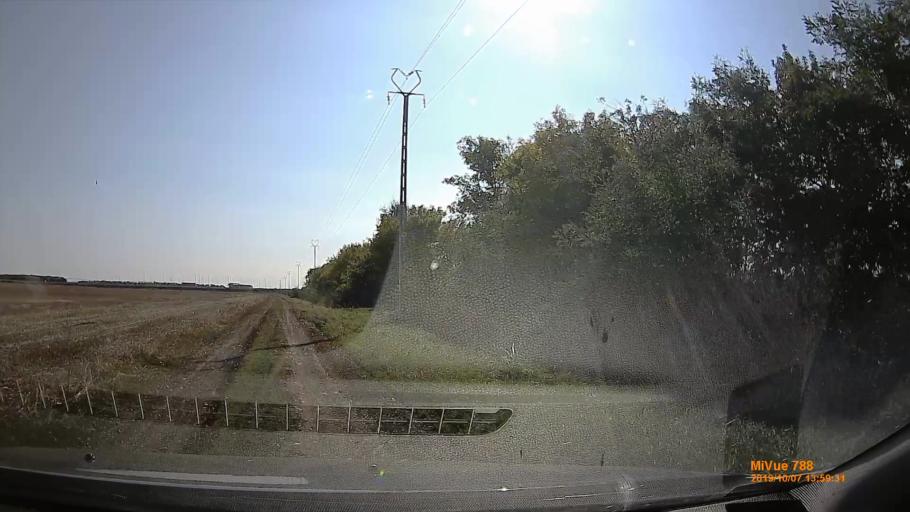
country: HU
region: Jasz-Nagykun-Szolnok
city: Cserkeszolo
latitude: 46.8892
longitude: 20.2144
